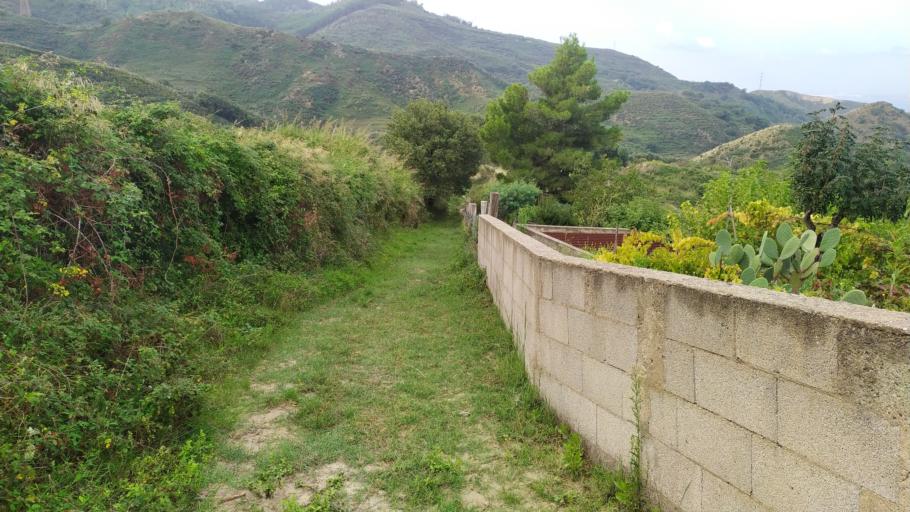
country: IT
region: Sicily
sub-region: Messina
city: Villafranca Tirrena
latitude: 38.2129
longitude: 15.4775
